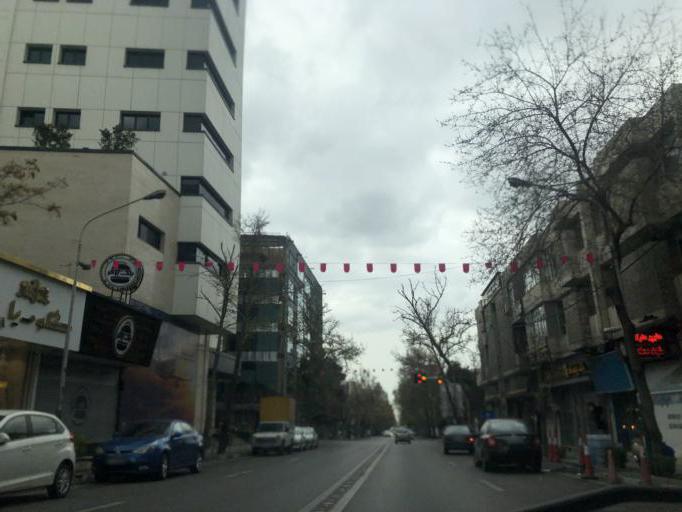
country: IR
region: Tehran
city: Tajrish
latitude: 35.7742
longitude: 51.4633
